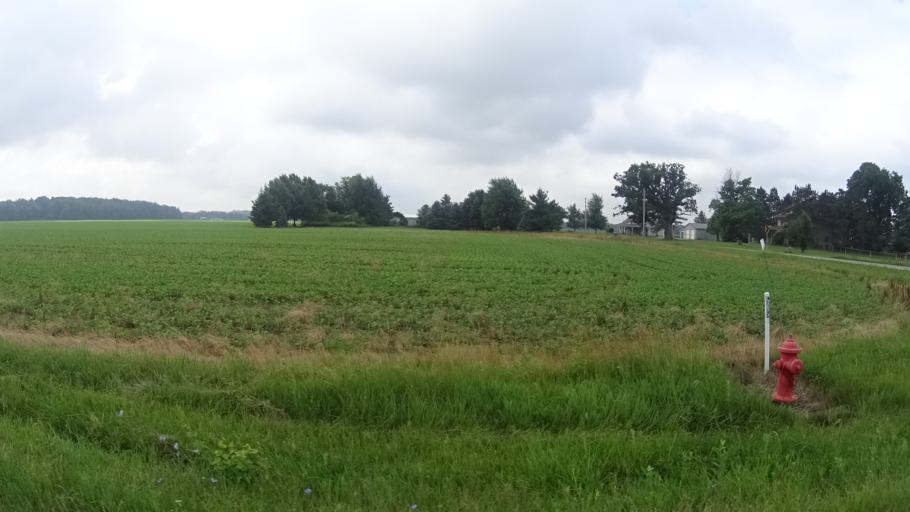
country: US
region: Ohio
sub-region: Huron County
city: Wakeman
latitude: 41.2848
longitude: -82.4915
